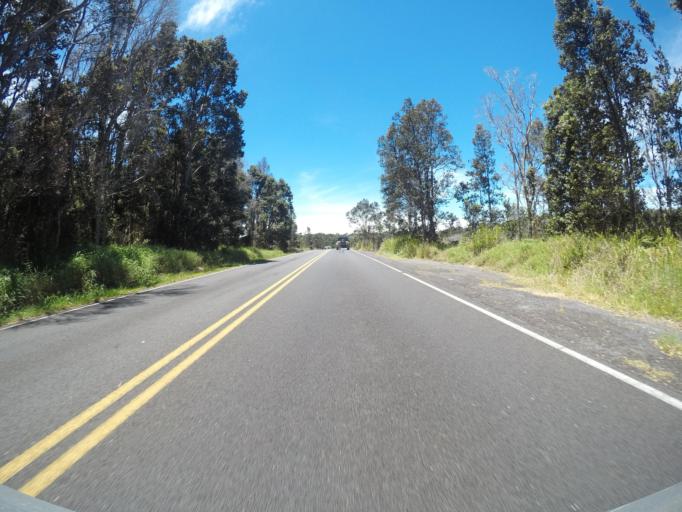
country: US
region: Hawaii
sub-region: Hawaii County
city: Volcano
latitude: 19.4007
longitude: -155.2534
